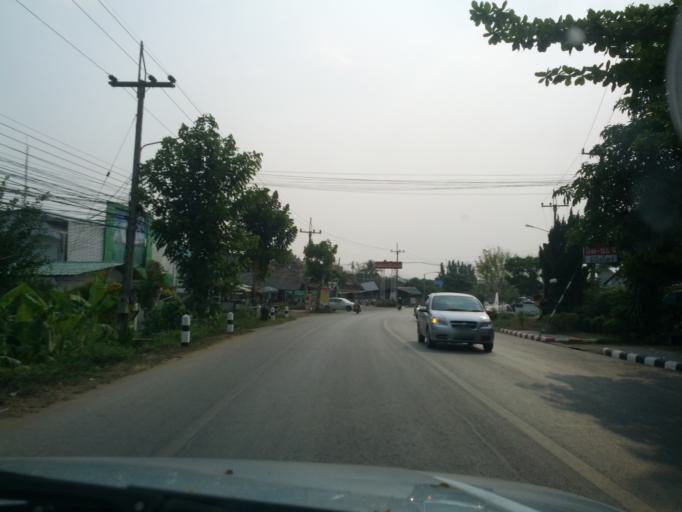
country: TH
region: Chiang Mai
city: Mae Taeng
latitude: 19.1451
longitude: 99.0027
